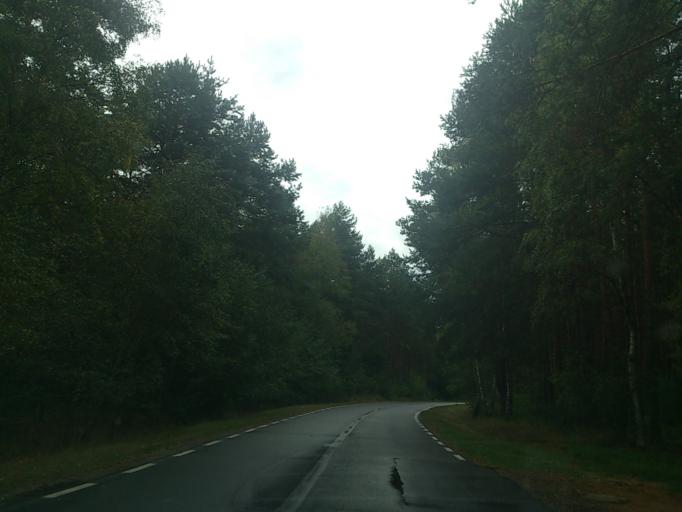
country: PL
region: Greater Poland Voivodeship
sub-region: Powiat gnieznienski
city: Kiszkowo
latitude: 52.5184
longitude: 17.1830
